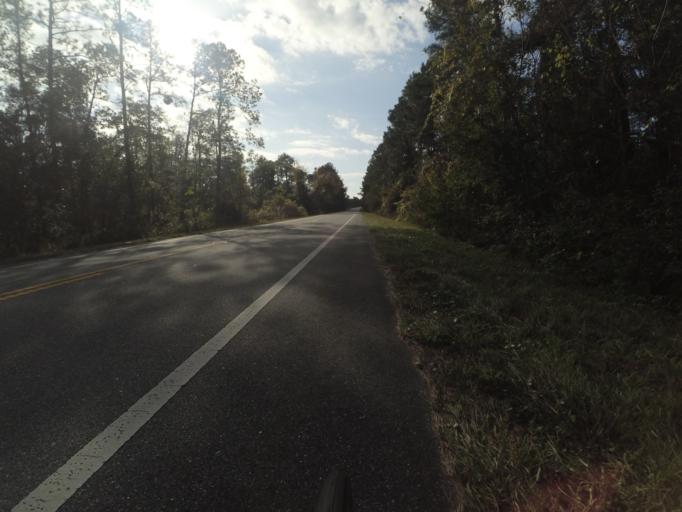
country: US
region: Florida
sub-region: Lake County
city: Astor
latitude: 29.1156
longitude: -81.6178
